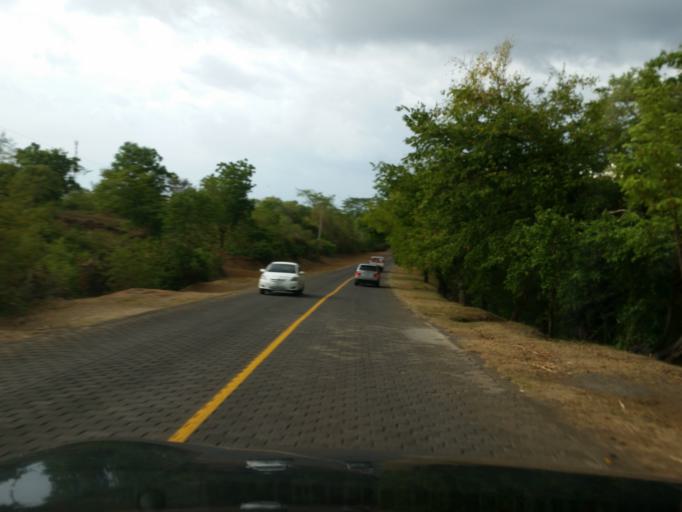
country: NI
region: Managua
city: Carlos Fonseca Amador
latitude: 11.9805
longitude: -86.5153
